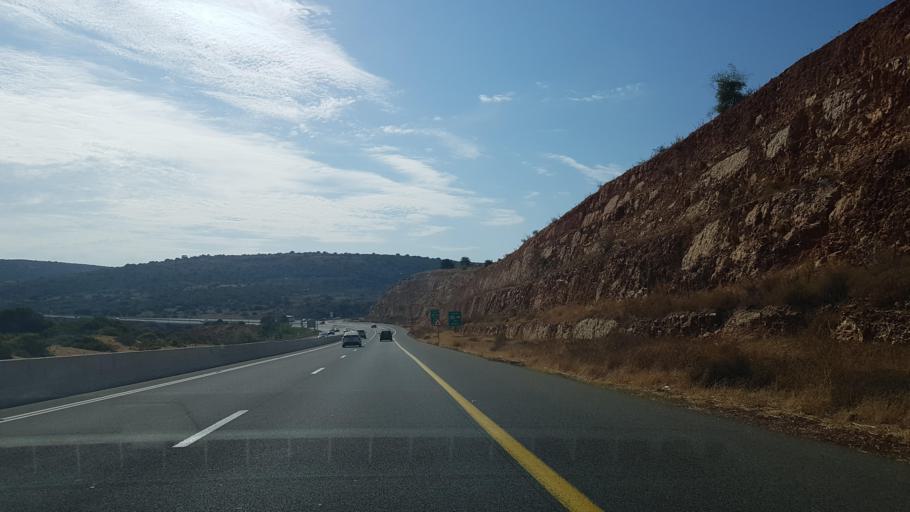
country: IL
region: Northern District
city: Maghar
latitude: 32.8693
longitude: 35.4602
